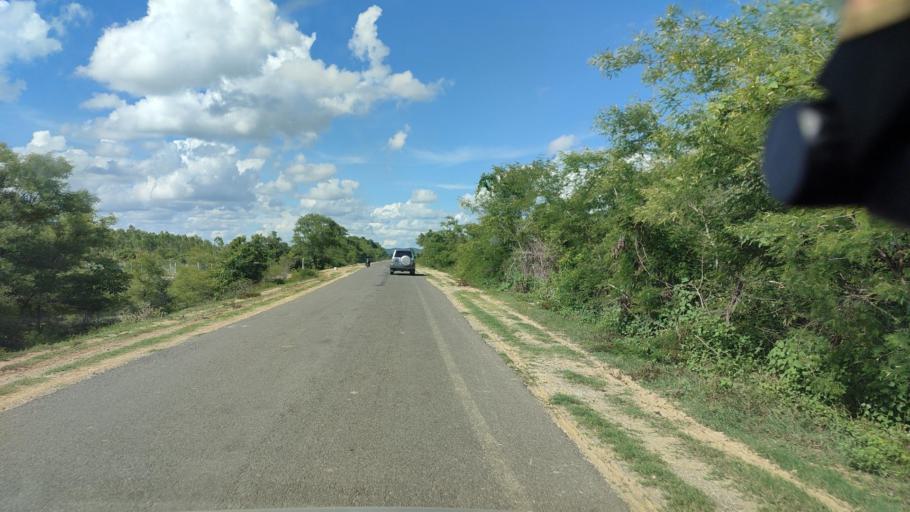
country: MM
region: Magway
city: Taungdwingyi
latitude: 20.1492
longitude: 95.5240
